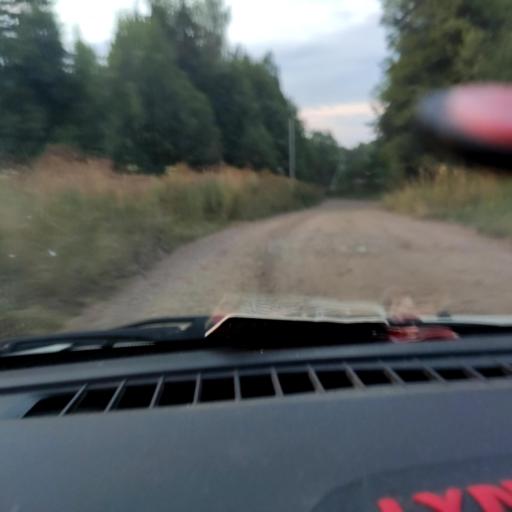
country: RU
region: Perm
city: Kukushtan
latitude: 57.6179
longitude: 56.4728
